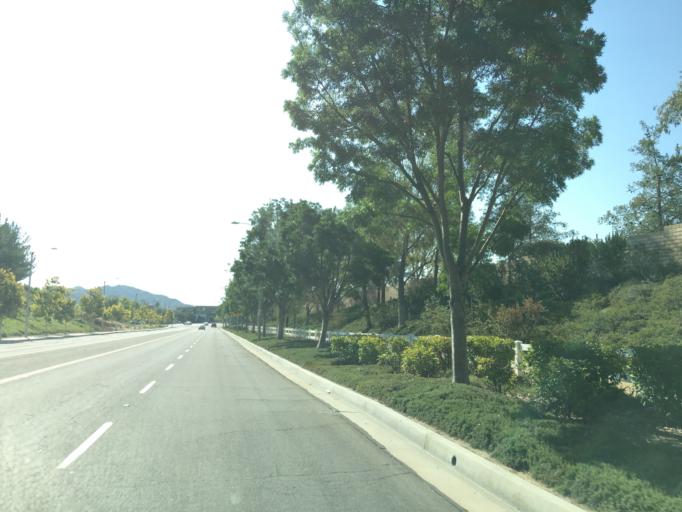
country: US
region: California
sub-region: Los Angeles County
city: Valencia
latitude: 34.4519
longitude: -118.6286
